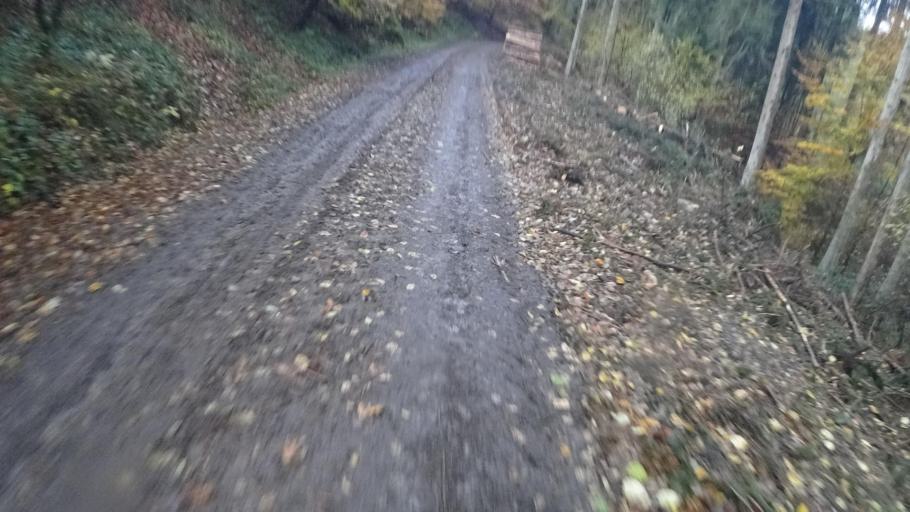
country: DE
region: Rheinland-Pfalz
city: Gondershausen
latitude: 50.1408
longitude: 7.4984
